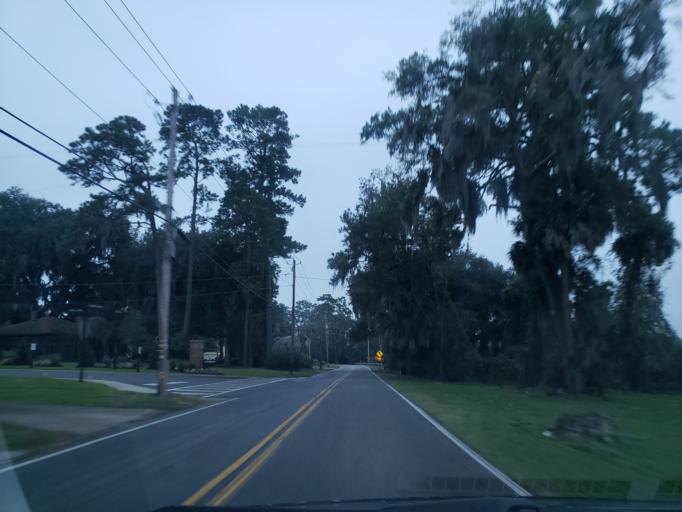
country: US
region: Georgia
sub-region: Chatham County
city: Isle of Hope
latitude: 32.0036
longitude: -81.0637
